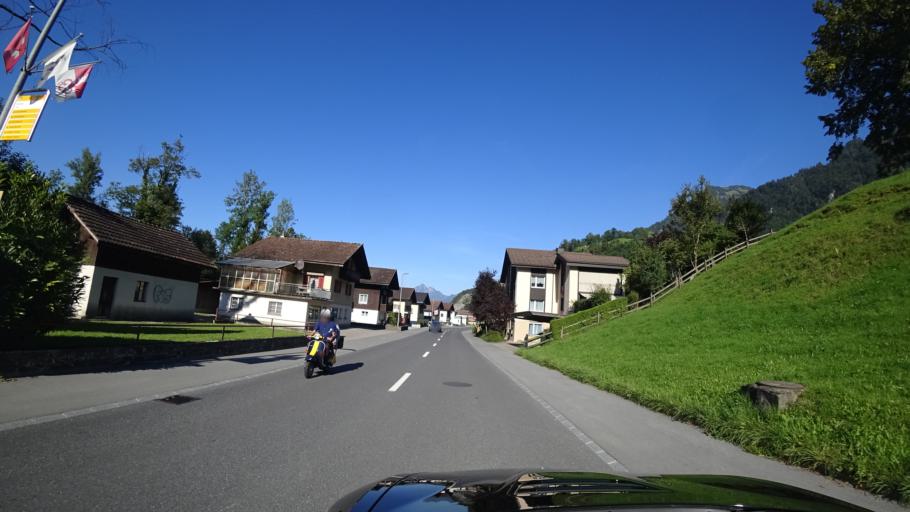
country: CH
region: Obwalden
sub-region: Obwalden
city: Giswil
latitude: 46.8324
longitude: 8.1792
